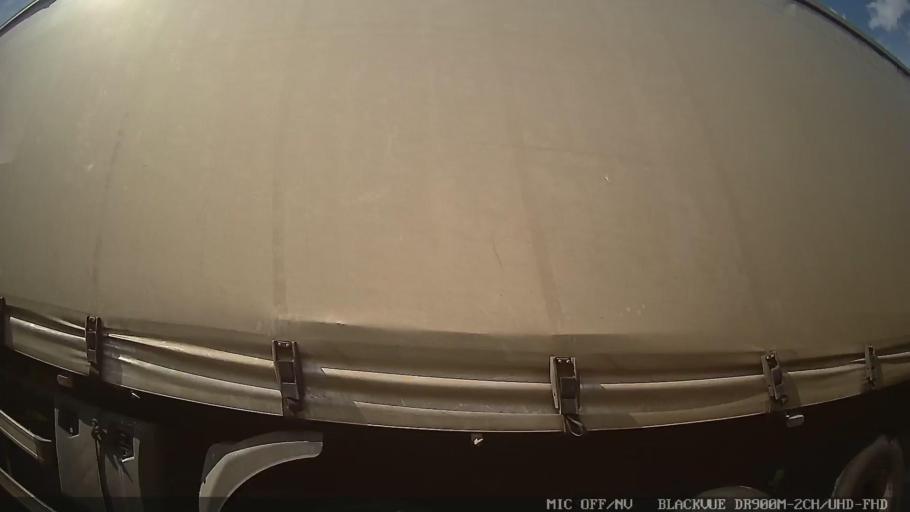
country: BR
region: Sao Paulo
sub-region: Atibaia
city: Atibaia
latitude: -23.0706
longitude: -46.5709
